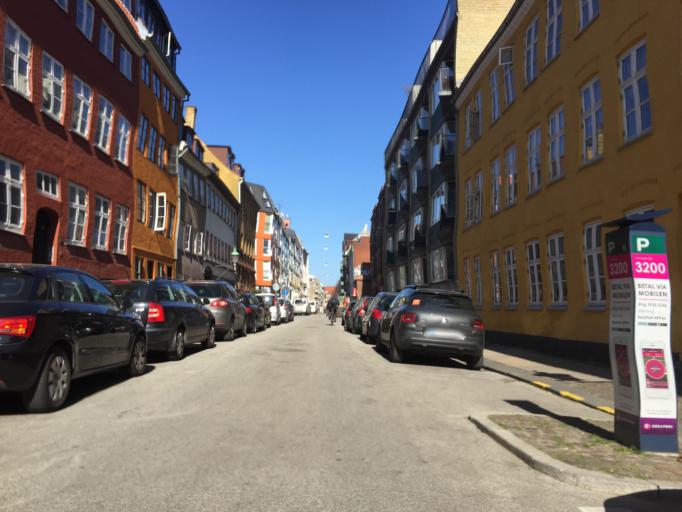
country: DK
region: Capital Region
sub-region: Kobenhavn
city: Christianshavn
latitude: 55.6708
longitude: 12.5898
